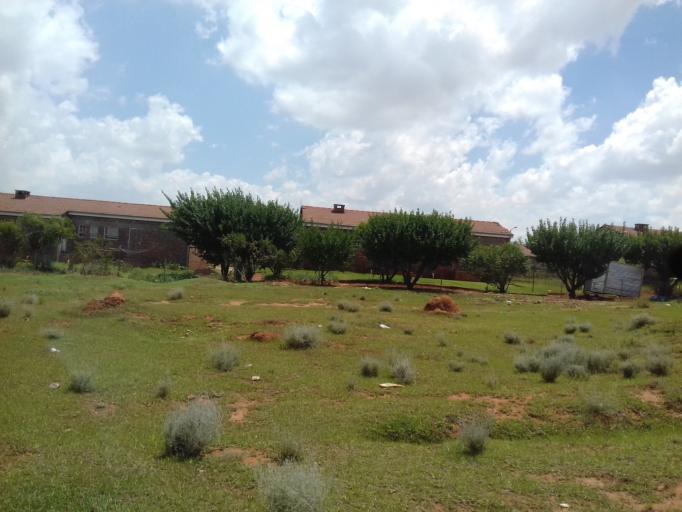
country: LS
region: Maseru
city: Maseru
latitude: -29.4509
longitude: 27.5634
